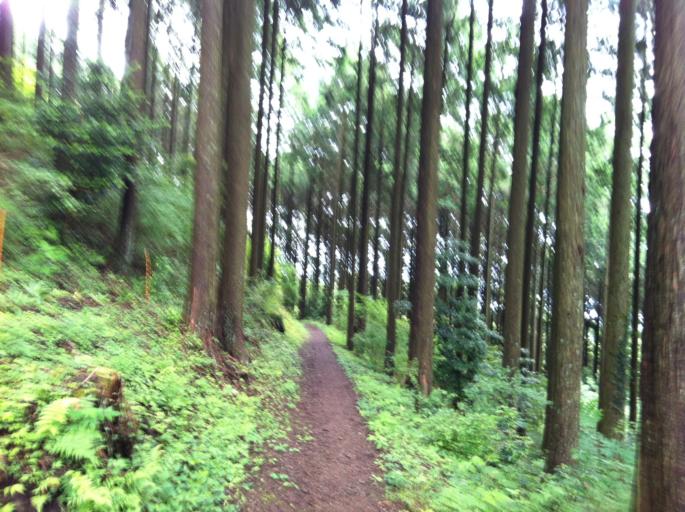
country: JP
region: Shizuoka
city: Shizuoka-shi
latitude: 35.0481
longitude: 138.3148
